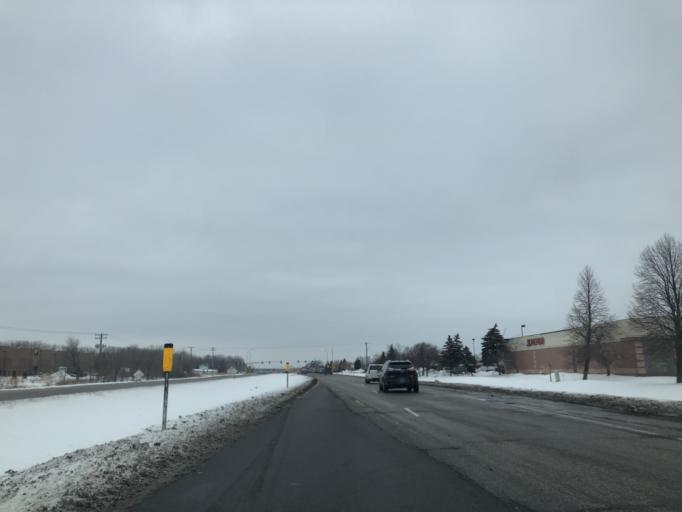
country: US
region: Minnesota
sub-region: Hennepin County
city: Brooklyn Park
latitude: 45.0921
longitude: -93.3826
